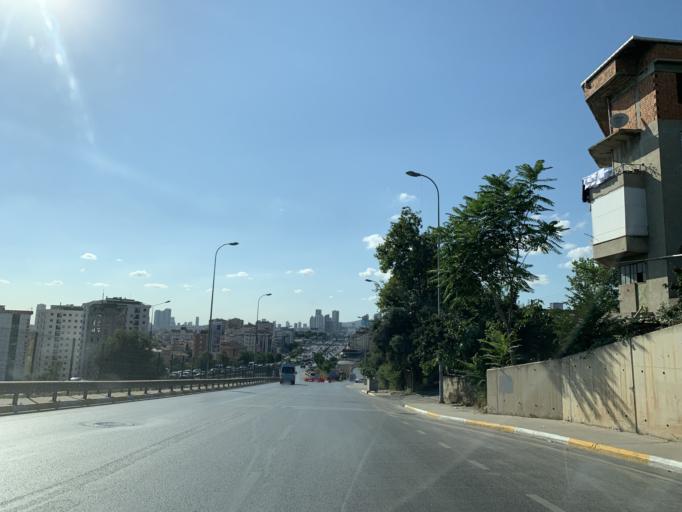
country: TR
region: Istanbul
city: Pendik
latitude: 40.8834
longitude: 29.2466
